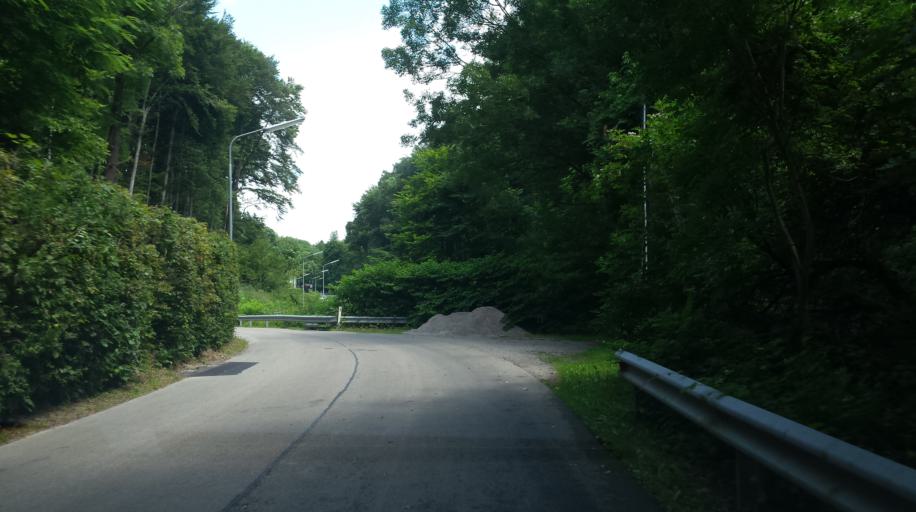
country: AT
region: Lower Austria
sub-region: Politischer Bezirk Wien-Umgebung
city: Mauerbach
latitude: 48.2429
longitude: 16.2104
